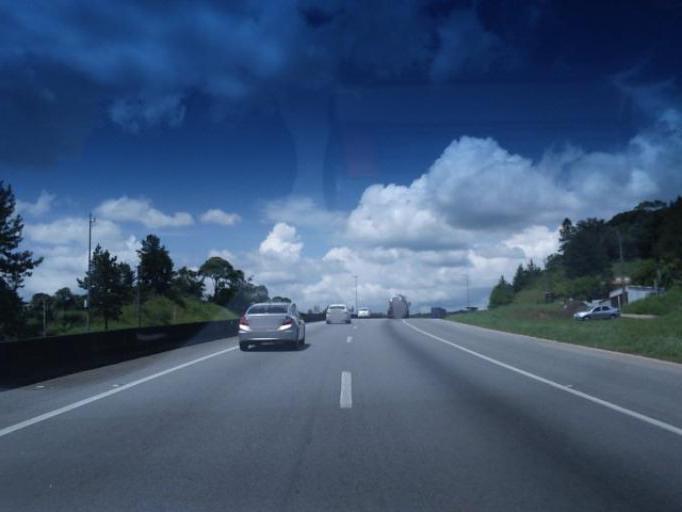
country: BR
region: Sao Paulo
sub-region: Juquitiba
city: Juquitiba
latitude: -23.9505
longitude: -47.1017
